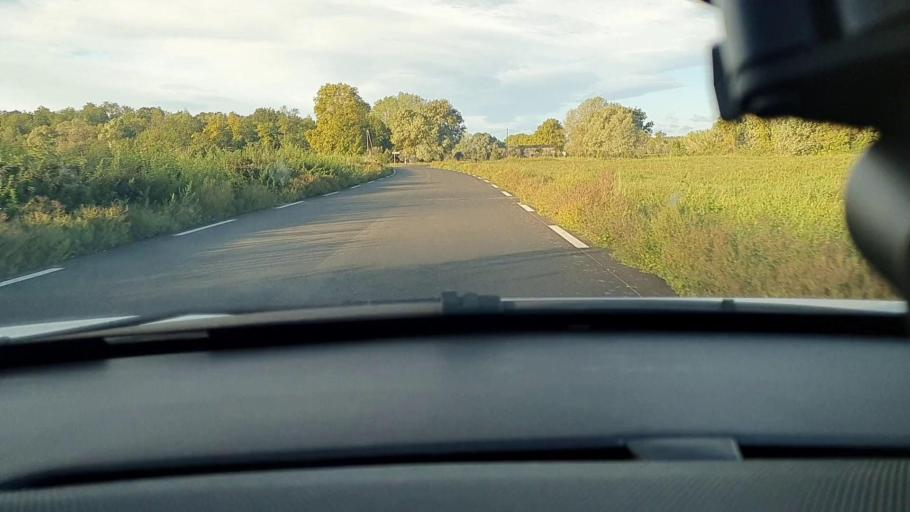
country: FR
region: Languedoc-Roussillon
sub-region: Departement du Gard
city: Saint-Ambroix
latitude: 44.2321
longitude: 4.2829
